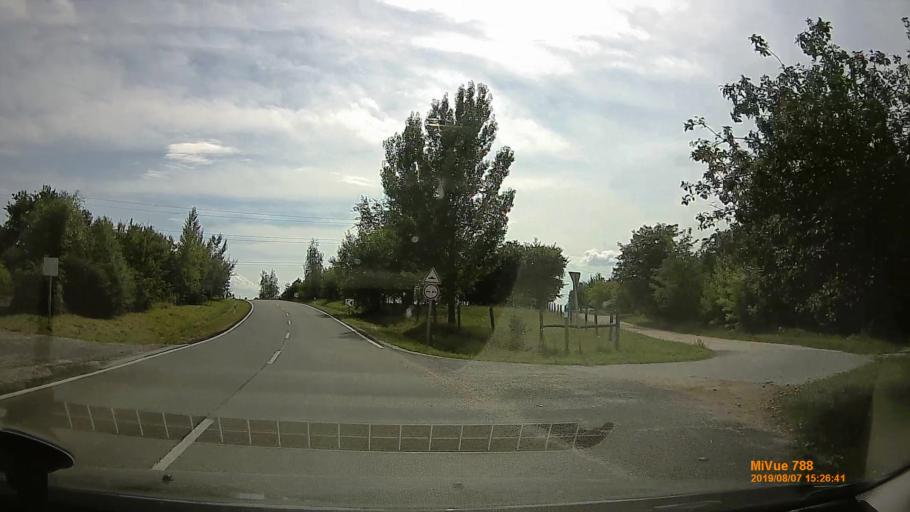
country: HU
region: Vas
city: Buk
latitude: 47.3027
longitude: 16.8243
